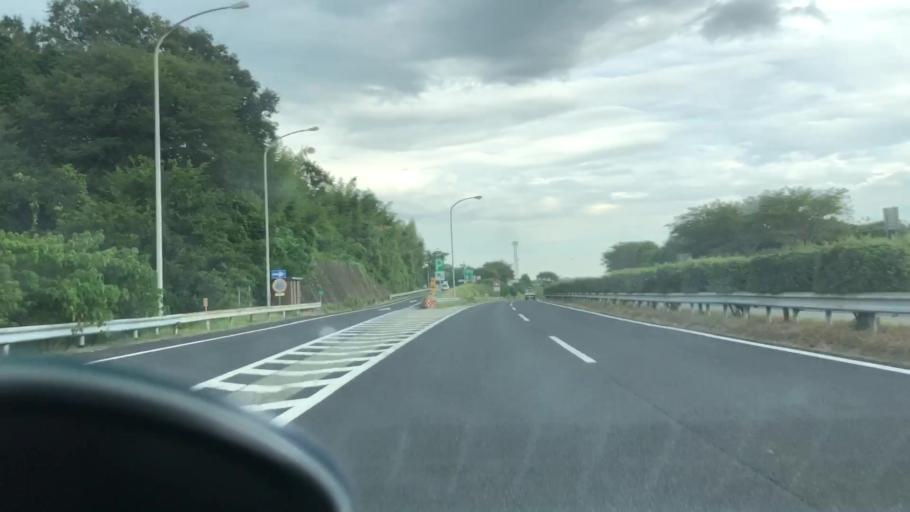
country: JP
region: Hyogo
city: Himeji
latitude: 34.9479
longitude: 134.7979
